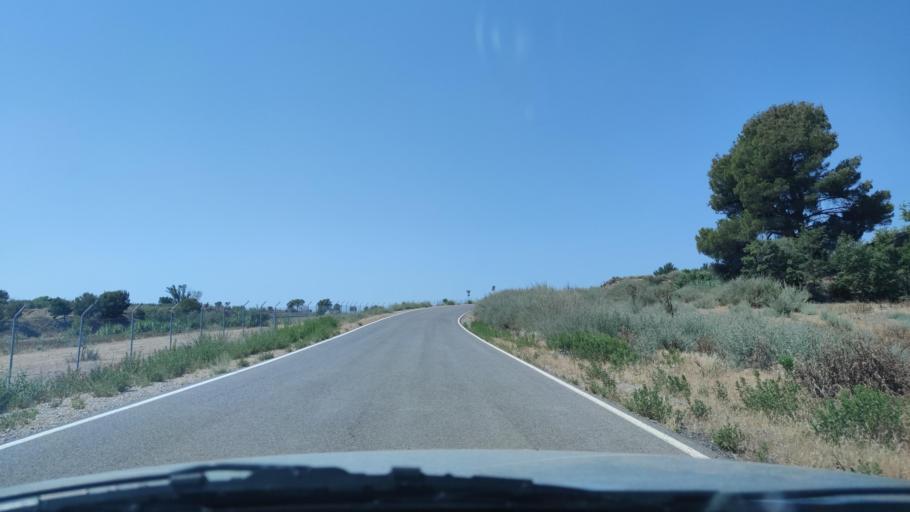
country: ES
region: Catalonia
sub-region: Provincia de Lleida
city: Alpicat
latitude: 41.6580
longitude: 0.5803
